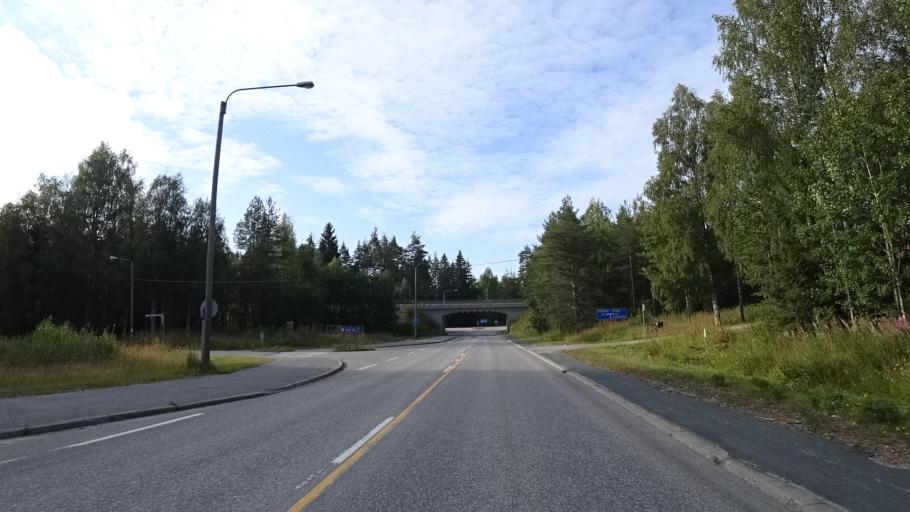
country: FI
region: North Karelia
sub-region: Joensuu
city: Eno
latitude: 62.8067
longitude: 30.1518
